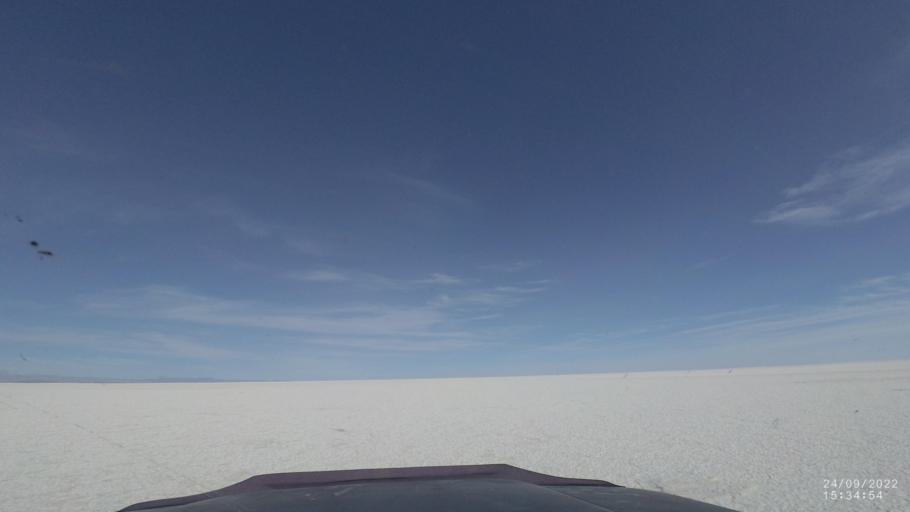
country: BO
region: Potosi
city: Colchani
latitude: -20.1291
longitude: -67.2586
